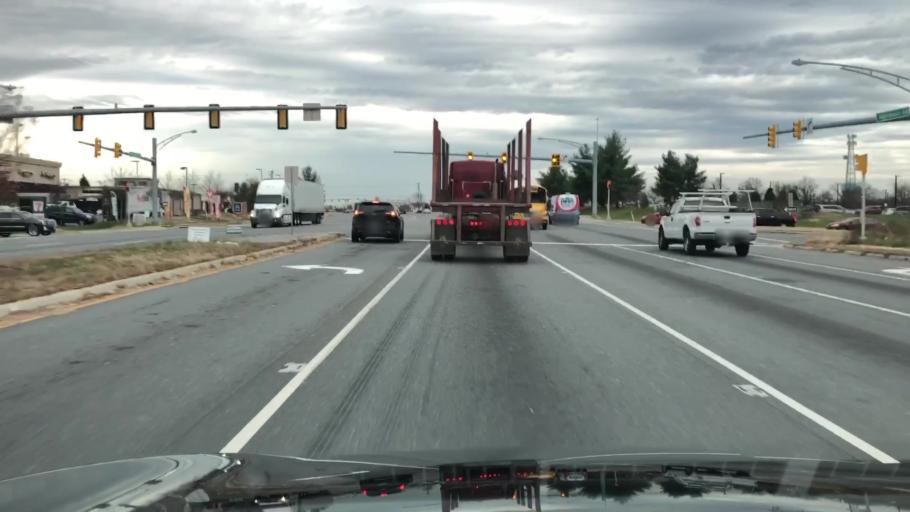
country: US
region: Virginia
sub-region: Stafford County
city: Falmouth
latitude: 38.3652
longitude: -77.5218
